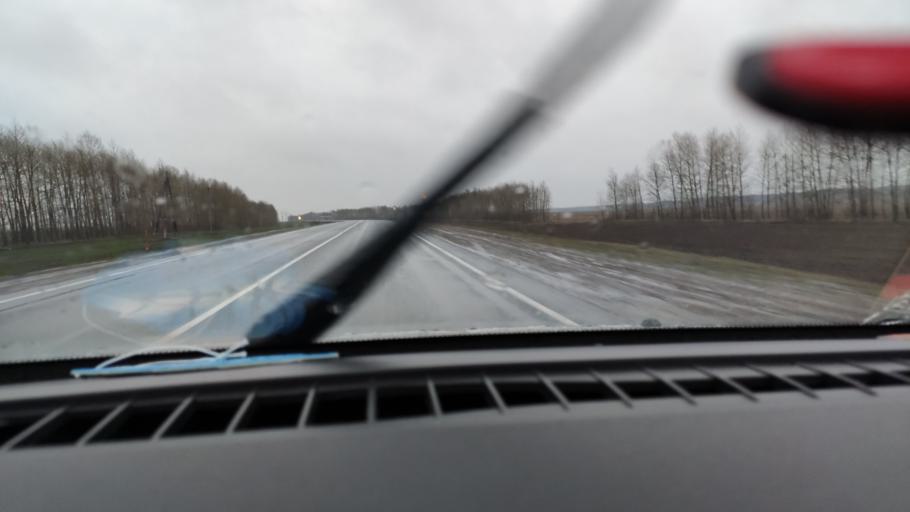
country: RU
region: Tatarstan
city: Mendeleyevsk
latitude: 55.9238
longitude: 52.2762
